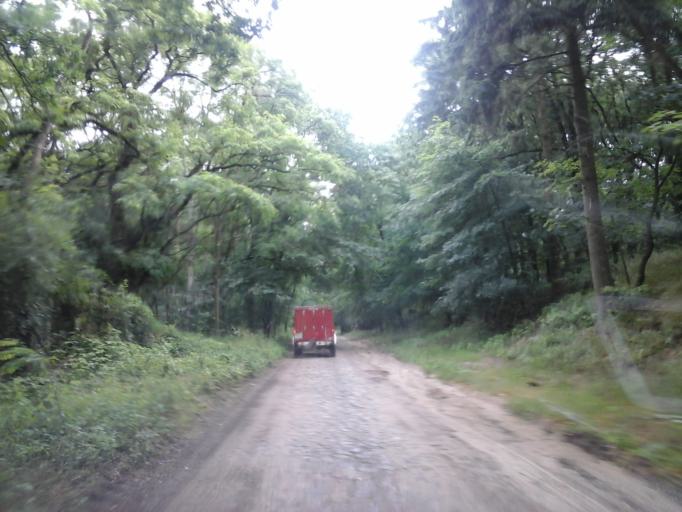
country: PL
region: West Pomeranian Voivodeship
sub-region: Powiat choszczenski
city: Bierzwnik
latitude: 52.9736
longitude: 15.6011
